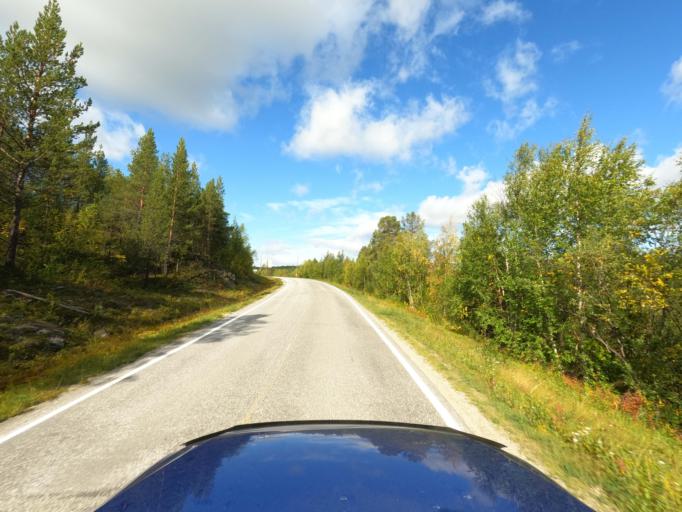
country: NO
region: Finnmark Fylke
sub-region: Karasjok
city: Karasjohka
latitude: 69.4812
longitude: 25.5161
